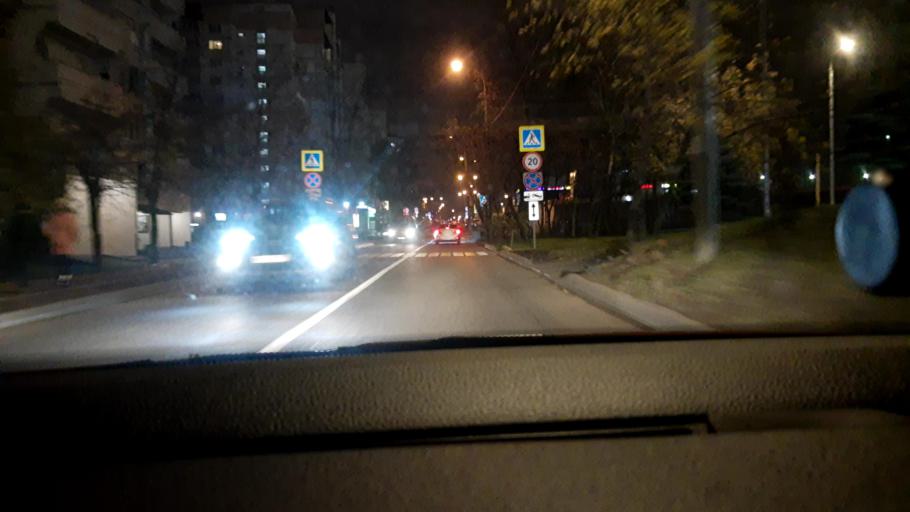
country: RU
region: Moscow
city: Ochakovo-Matveyevskoye
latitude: 55.6830
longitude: 37.4526
